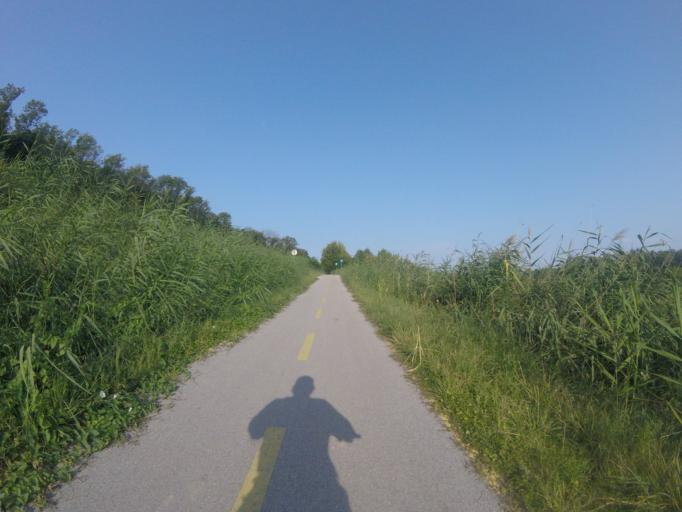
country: HU
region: Gyor-Moson-Sopron
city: Nagycenk
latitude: 47.6329
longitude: 16.7209
